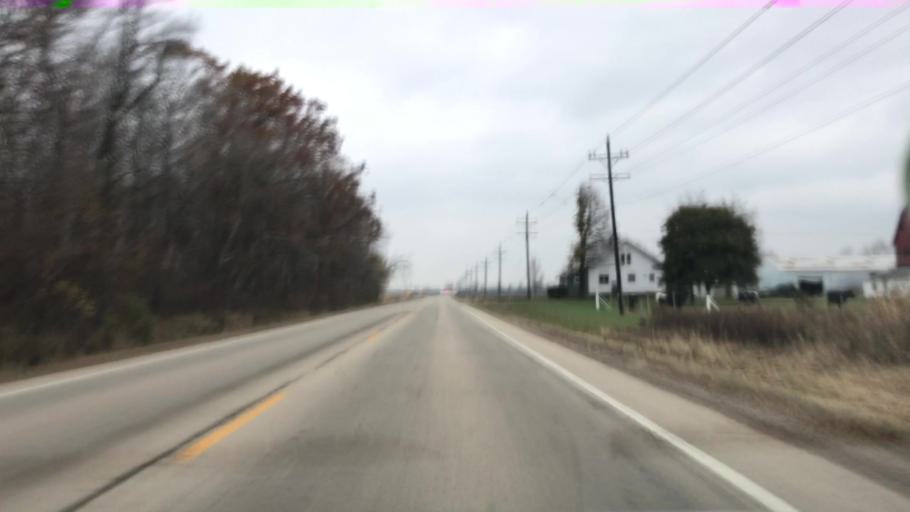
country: US
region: Wisconsin
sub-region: Outagamie County
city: Seymour
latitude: 44.4926
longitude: -88.2912
